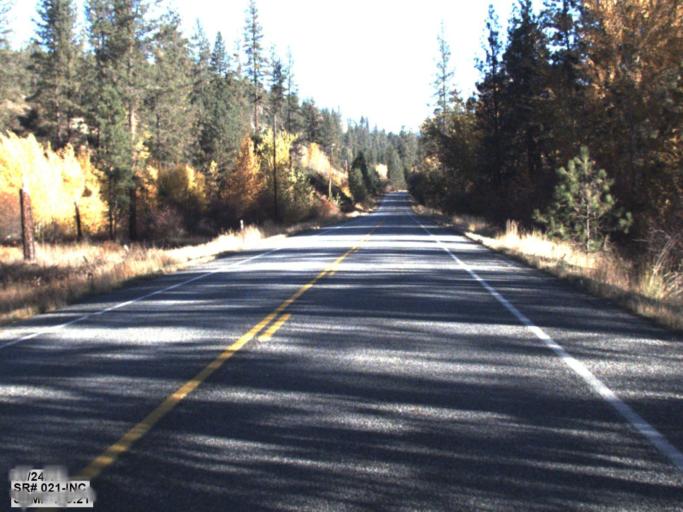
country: US
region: Washington
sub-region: Okanogan County
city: Coulee Dam
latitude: 48.1107
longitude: -118.6991
